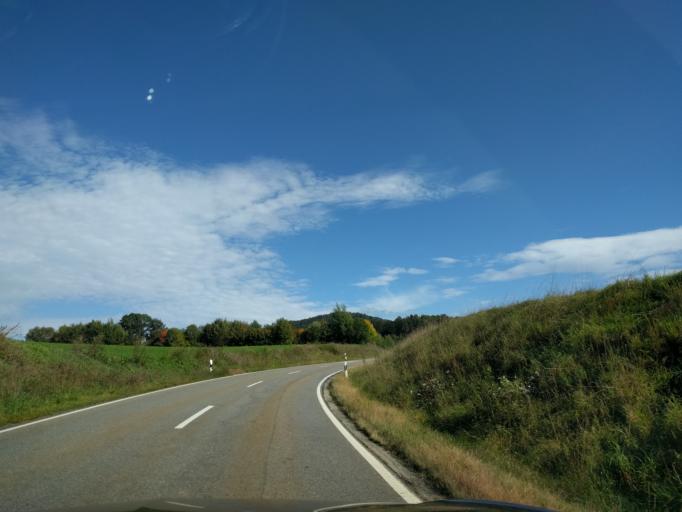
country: DE
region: Bavaria
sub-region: Lower Bavaria
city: Viechtach
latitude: 49.0947
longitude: 12.8843
